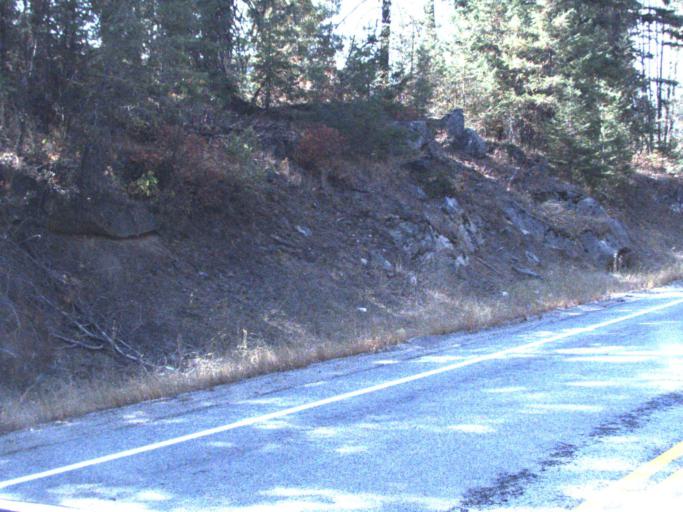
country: US
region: Washington
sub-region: Pend Oreille County
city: Newport
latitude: 48.1263
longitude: -117.2753
